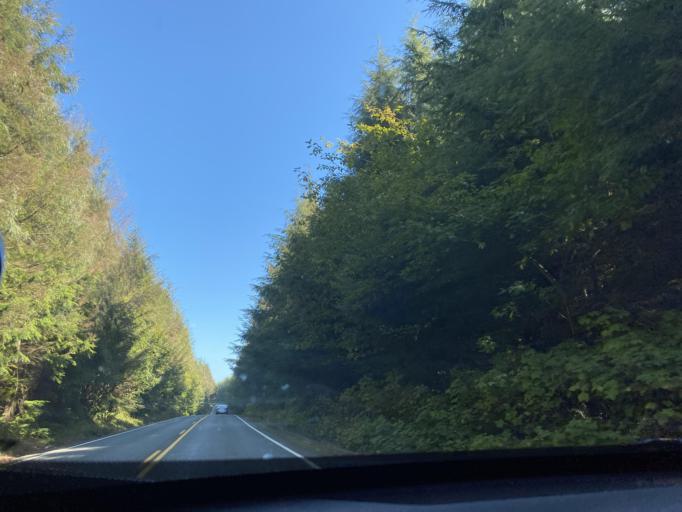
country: US
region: Washington
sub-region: Clallam County
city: Forks
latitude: 47.9194
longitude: -124.5162
